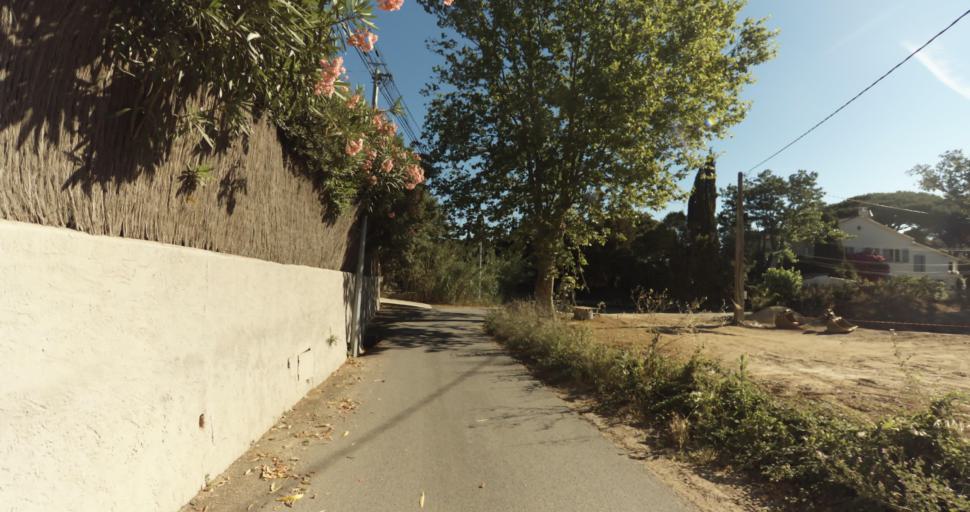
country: FR
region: Provence-Alpes-Cote d'Azur
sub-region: Departement du Var
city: Saint-Tropez
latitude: 43.2616
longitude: 6.6215
